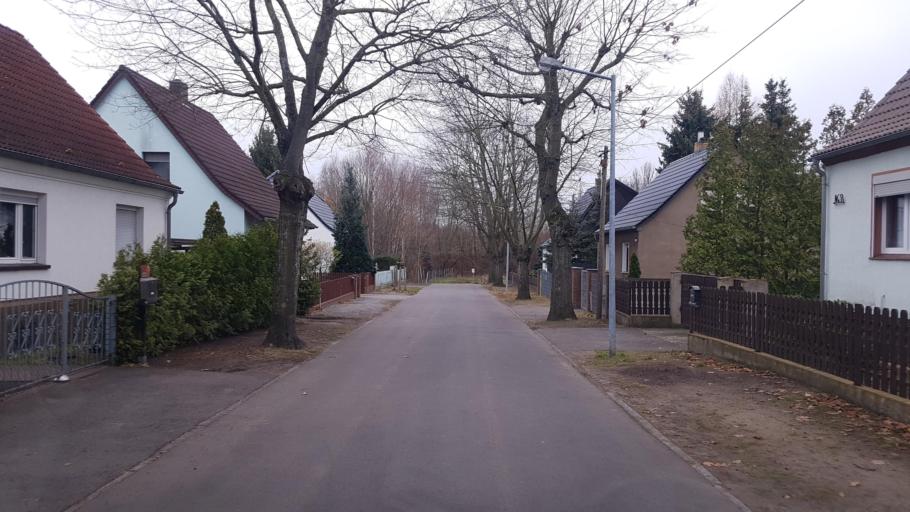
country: DE
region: Brandenburg
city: Lauchhammer
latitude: 51.4687
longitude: 13.7920
